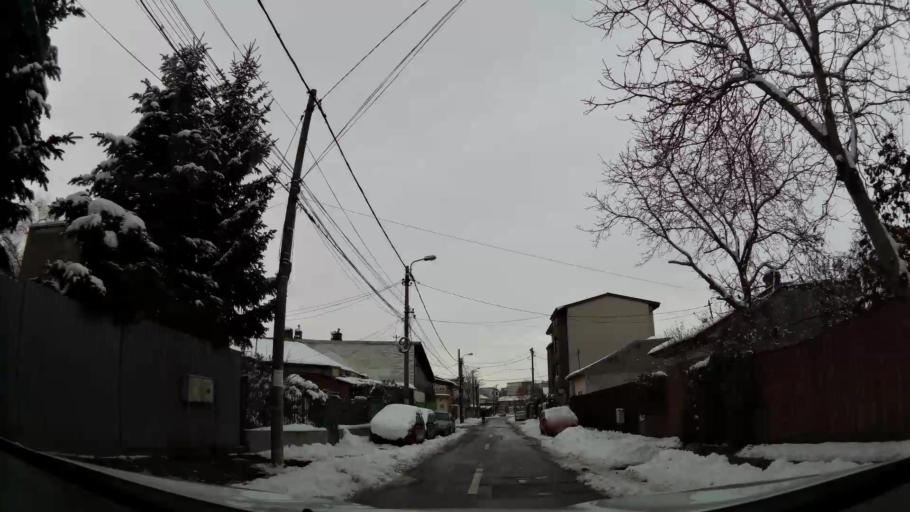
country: RO
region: Bucuresti
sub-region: Municipiul Bucuresti
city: Bucuresti
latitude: 44.3891
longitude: 26.0968
